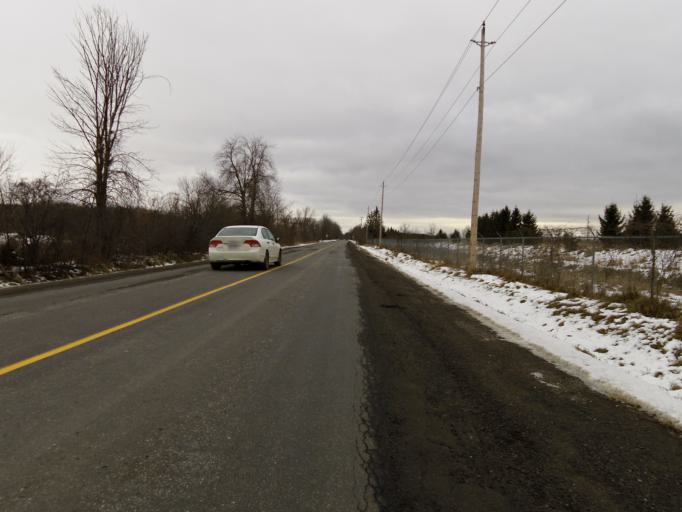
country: CA
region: Ontario
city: Bells Corners
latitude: 45.3619
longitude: -75.9174
